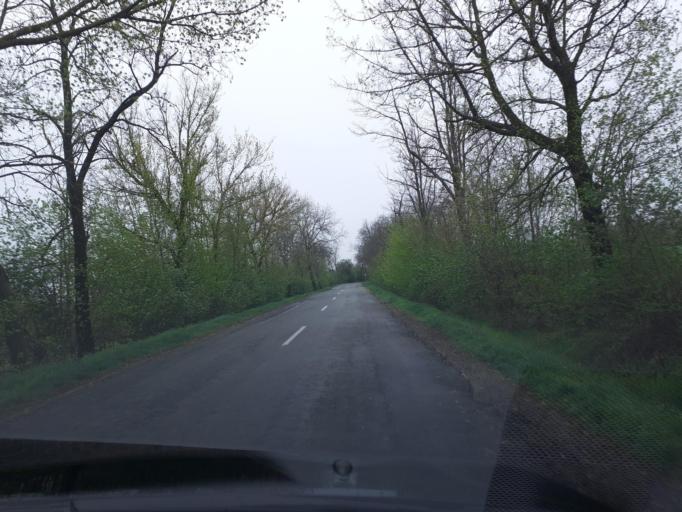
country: HU
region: Tolna
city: Hogyesz
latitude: 46.4509
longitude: 18.4692
